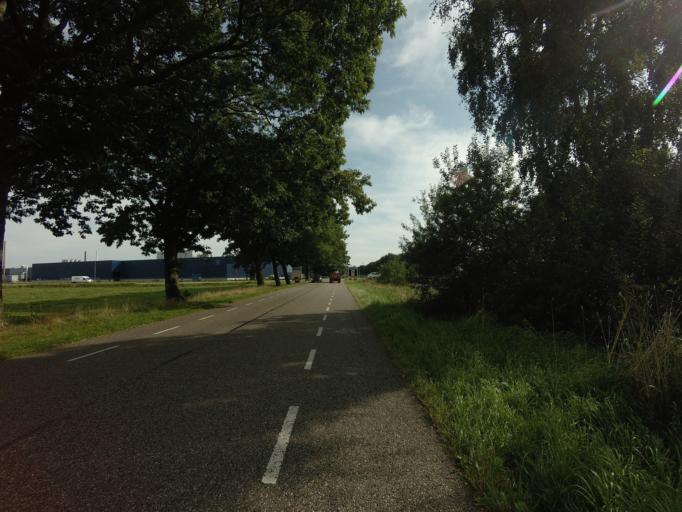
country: NL
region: Drenthe
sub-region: Gemeente Coevorden
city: Coevorden
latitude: 52.6683
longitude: 6.7257
